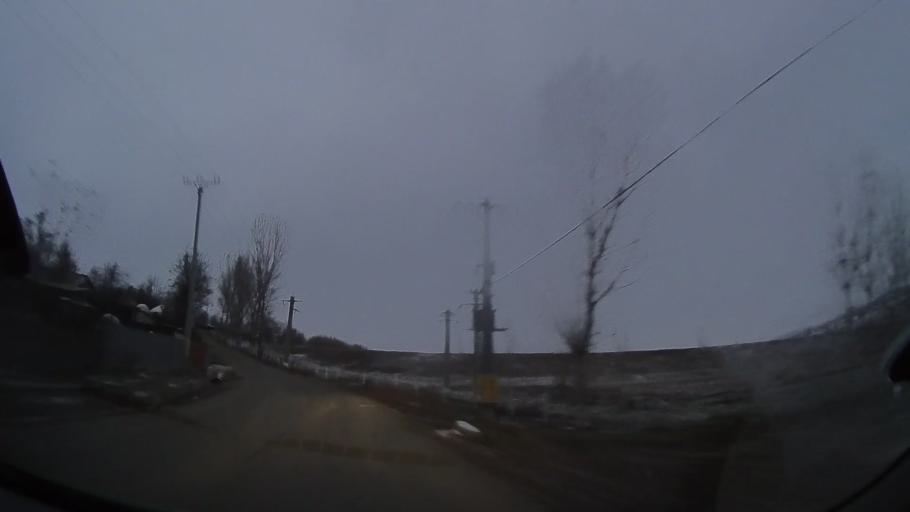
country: RO
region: Vaslui
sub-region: Comuna Vutcani
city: Vutcani
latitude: 46.4166
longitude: 27.9979
